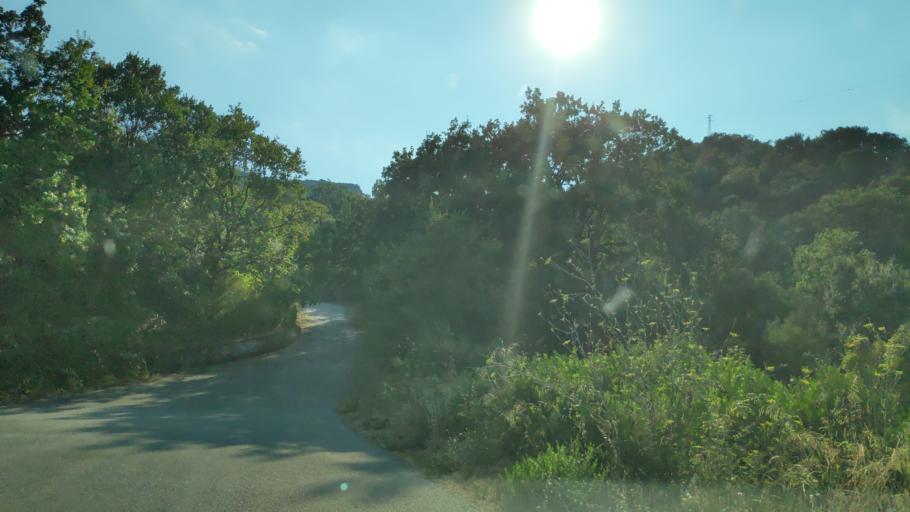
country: IT
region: Calabria
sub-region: Provincia di Reggio Calabria
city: Placanica
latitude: 38.4129
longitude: 16.4400
